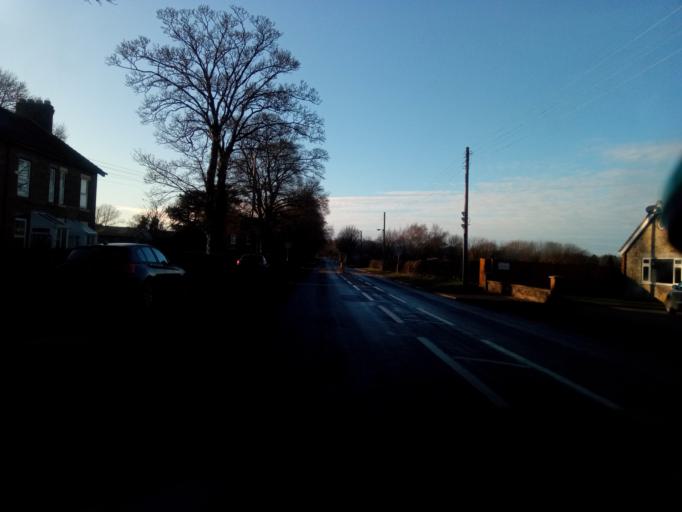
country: GB
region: England
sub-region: North Yorkshire
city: Thirsk
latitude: 54.2275
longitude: -1.3802
